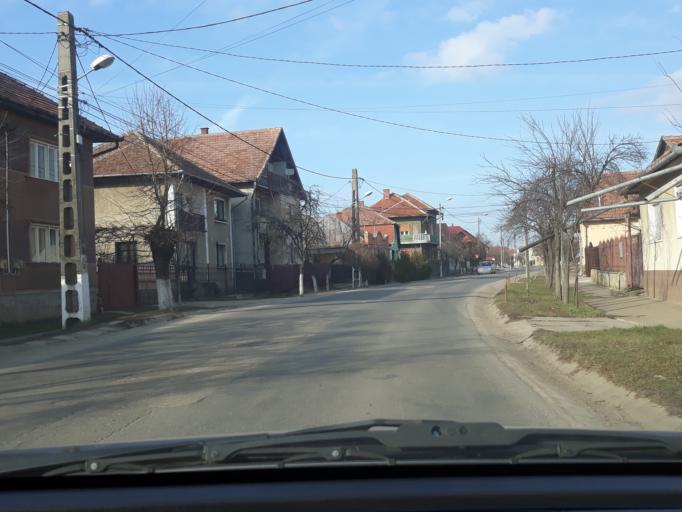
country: RO
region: Bihor
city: Margita
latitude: 47.3508
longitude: 22.3391
